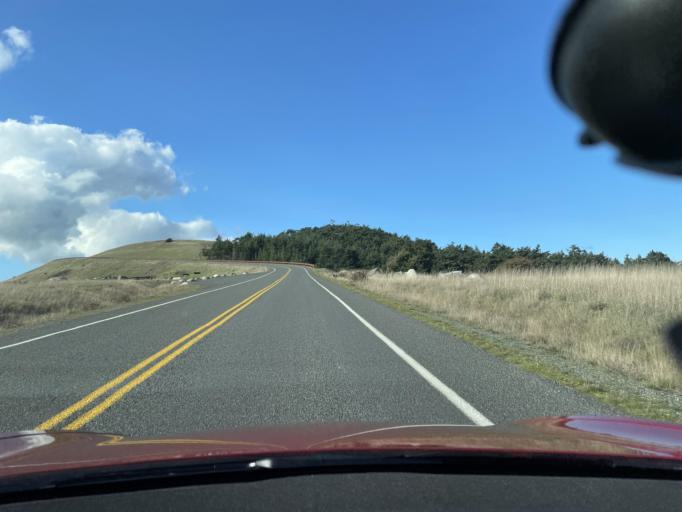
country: US
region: Washington
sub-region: San Juan County
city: Friday Harbor
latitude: 48.4538
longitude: -122.9702
